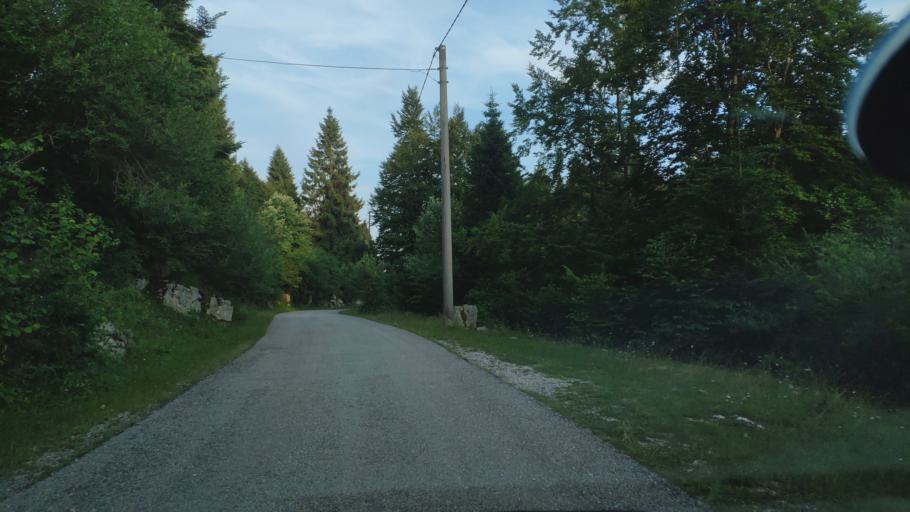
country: IT
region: Veneto
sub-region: Provincia di Vicenza
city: Calvene
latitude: 45.8003
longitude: 11.5181
